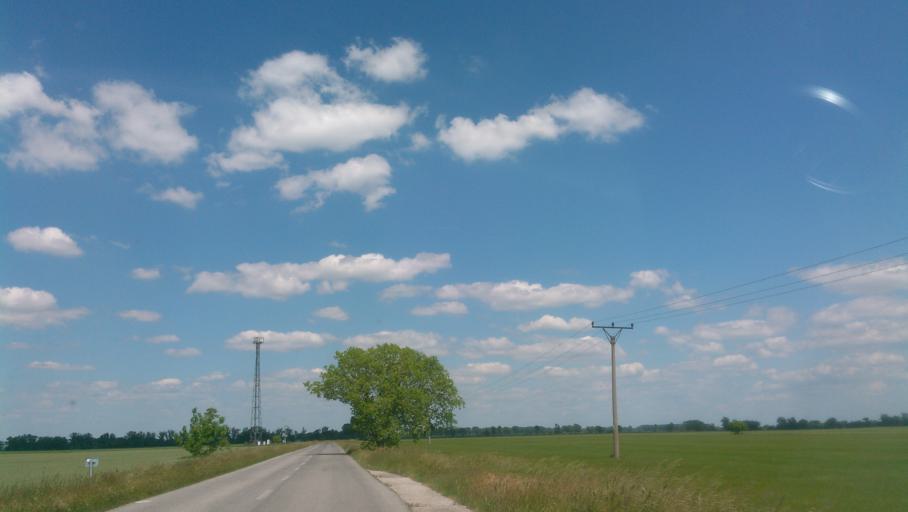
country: SK
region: Trnavsky
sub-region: Okres Dunajska Streda
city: Velky Meder
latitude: 47.8837
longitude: 17.8213
